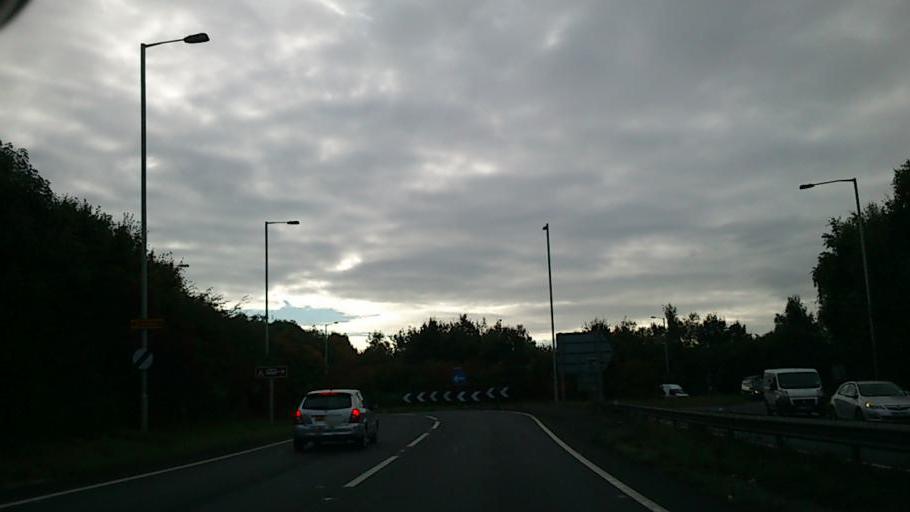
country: GB
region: England
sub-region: Shropshire
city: Great Hanwood
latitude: 52.7039
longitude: -2.8110
